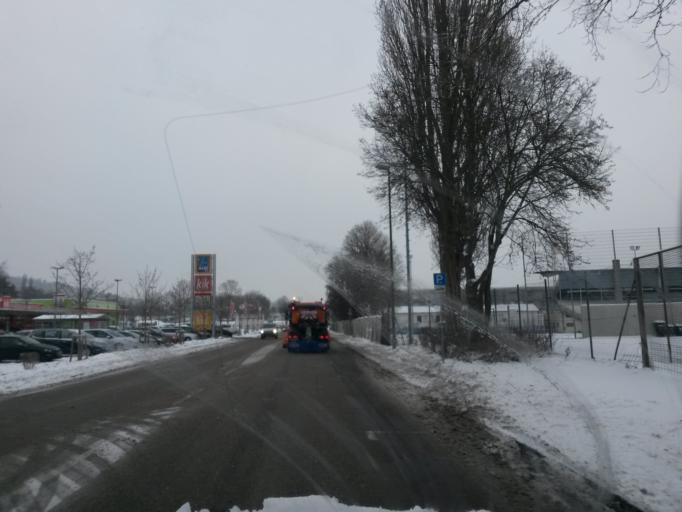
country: DE
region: Baden-Wuerttemberg
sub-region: Karlsruhe Region
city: Birkenfeld
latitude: 48.8821
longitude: 8.6594
